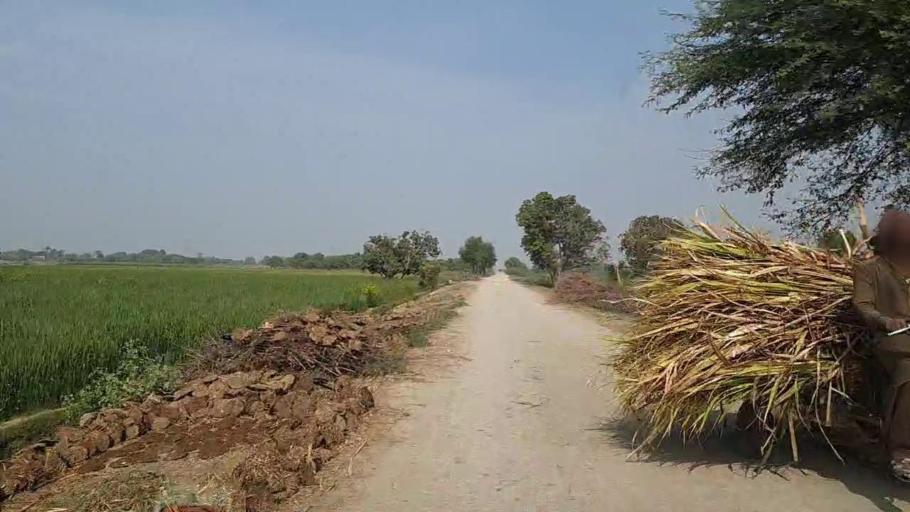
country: PK
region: Sindh
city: Mirwah Gorchani
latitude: 25.3449
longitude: 69.0637
